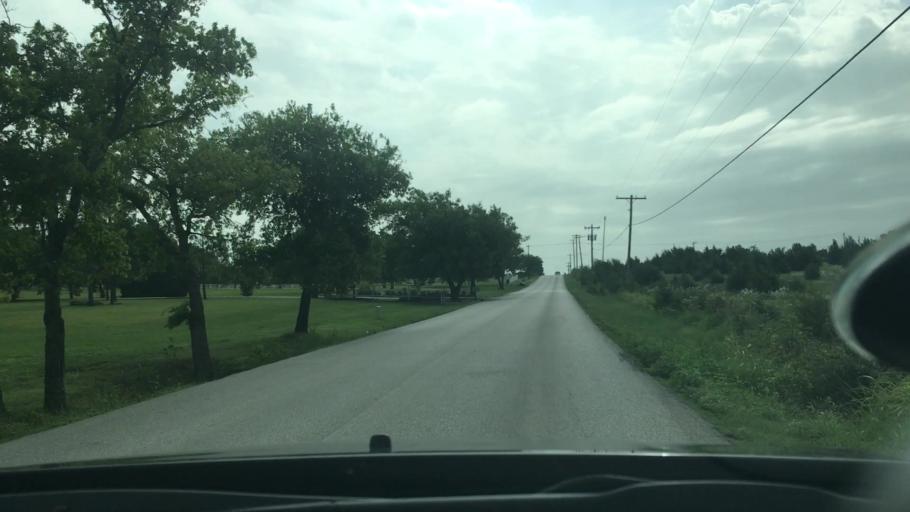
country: US
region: Oklahoma
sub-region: Carter County
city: Ardmore
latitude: 34.2020
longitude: -97.1811
